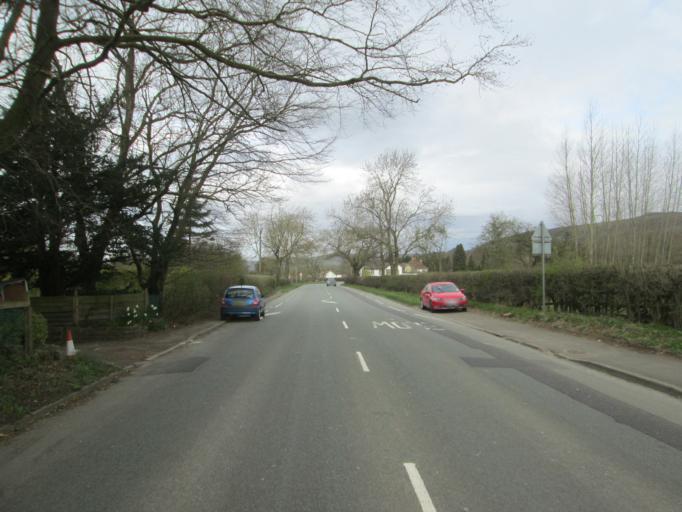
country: GB
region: England
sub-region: Derbyshire
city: Hathersage
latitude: 53.3405
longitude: -1.6982
